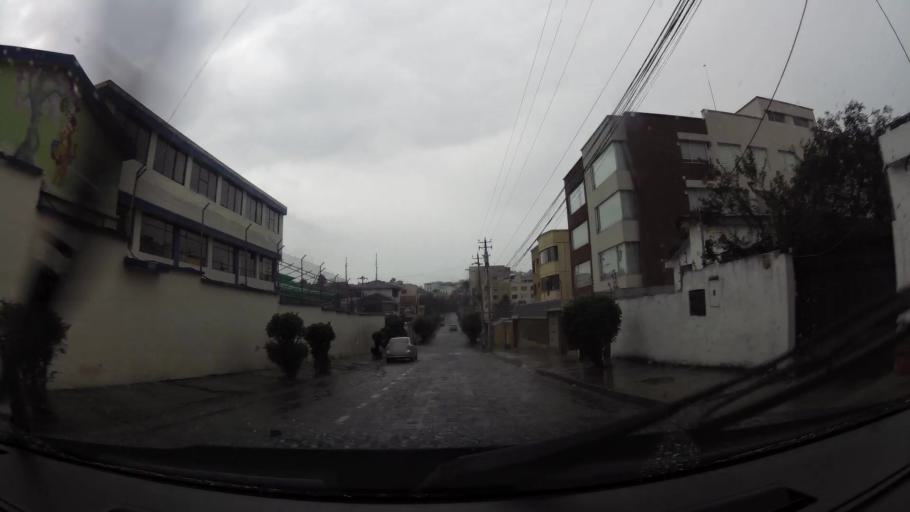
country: EC
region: Pichincha
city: Quito
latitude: -0.1558
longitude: -78.4613
